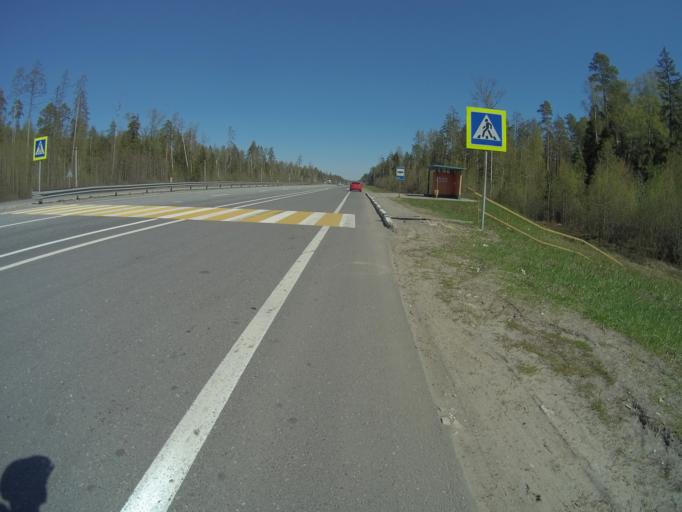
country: RU
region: Vladimir
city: Orgtrud
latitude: 56.0986
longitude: 40.5827
